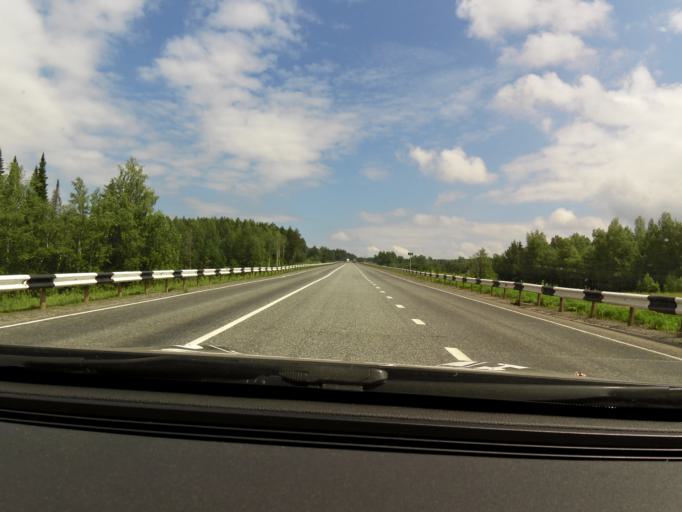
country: RU
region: Perm
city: Suksun
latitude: 57.0921
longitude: 57.3712
